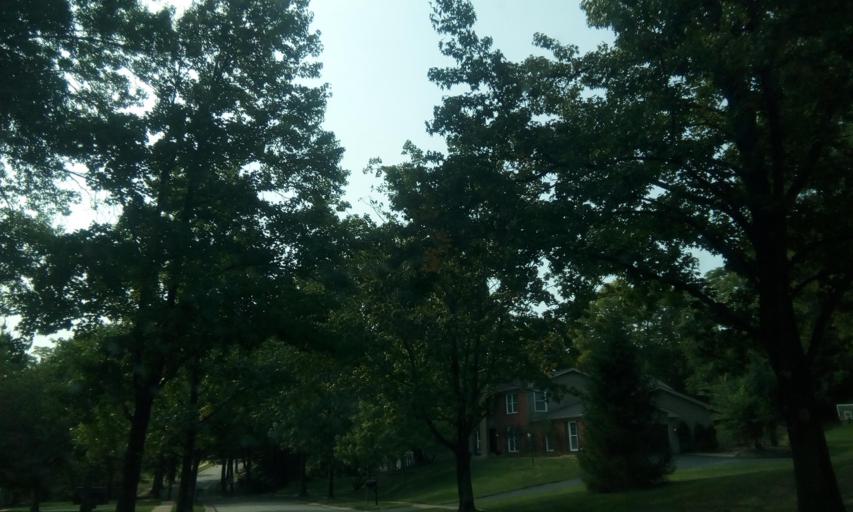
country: US
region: Missouri
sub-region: Saint Louis County
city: Town and Country
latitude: 38.6143
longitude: -90.4795
